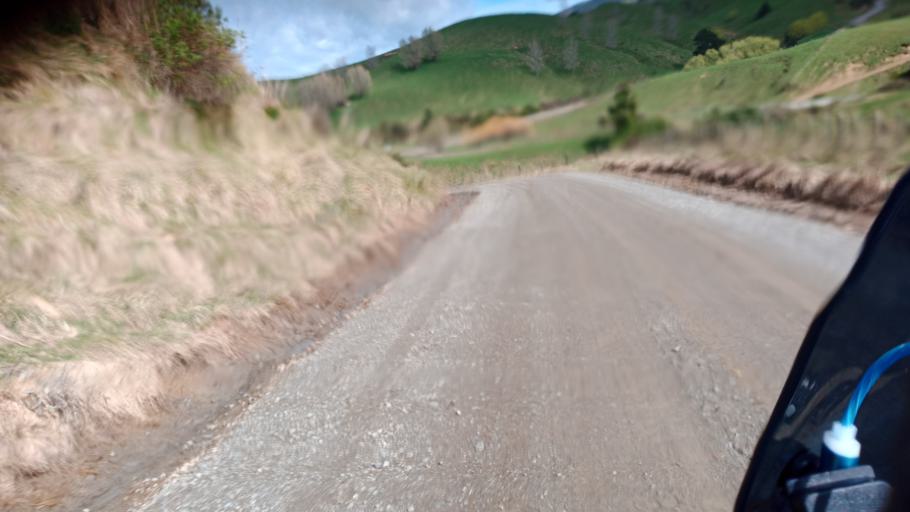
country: NZ
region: Hawke's Bay
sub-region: Wairoa District
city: Wairoa
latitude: -38.7392
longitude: 177.2928
